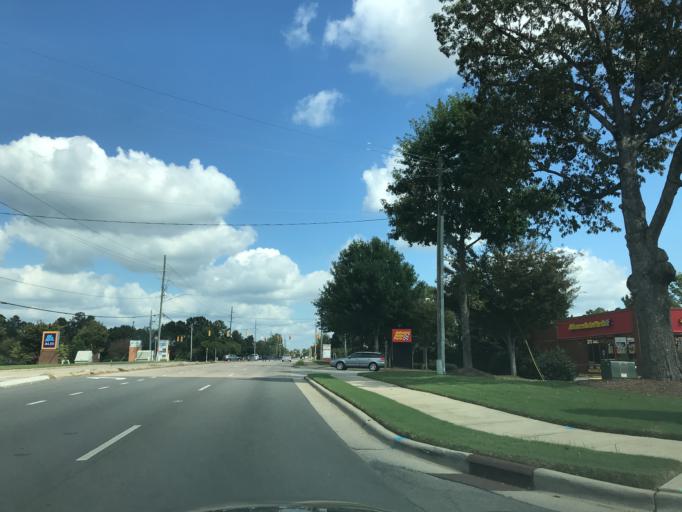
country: US
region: North Carolina
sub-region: Wake County
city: Wake Forest
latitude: 35.9475
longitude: -78.5355
